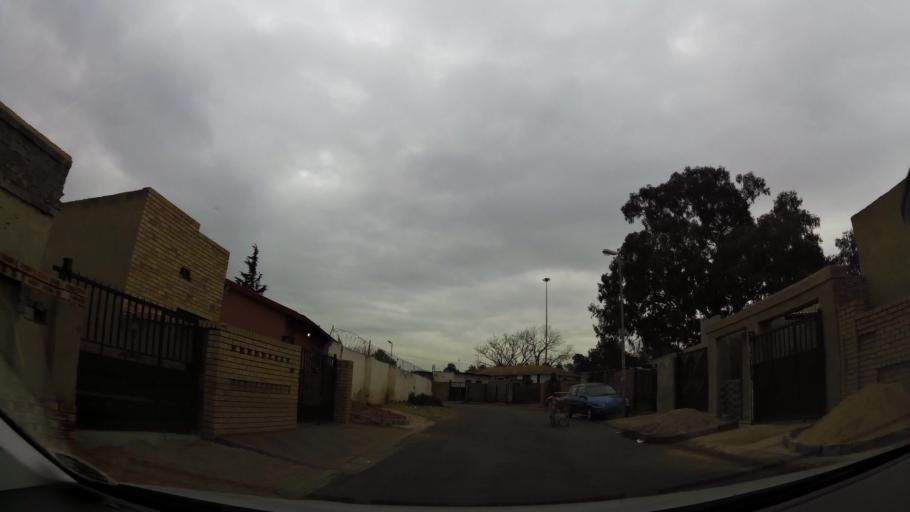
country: ZA
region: Gauteng
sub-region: City of Johannesburg Metropolitan Municipality
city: Soweto
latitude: -26.2536
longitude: 27.8754
